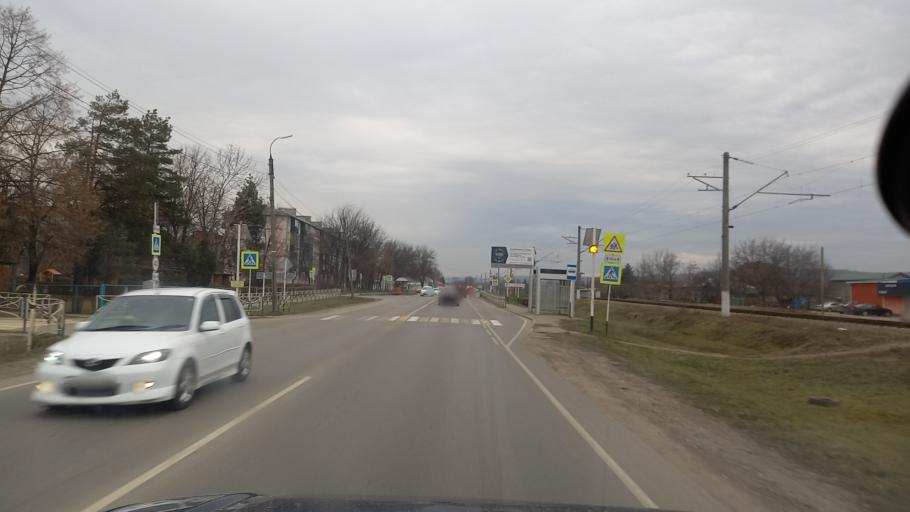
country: RU
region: Adygeya
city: Maykop
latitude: 44.5967
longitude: 40.1324
